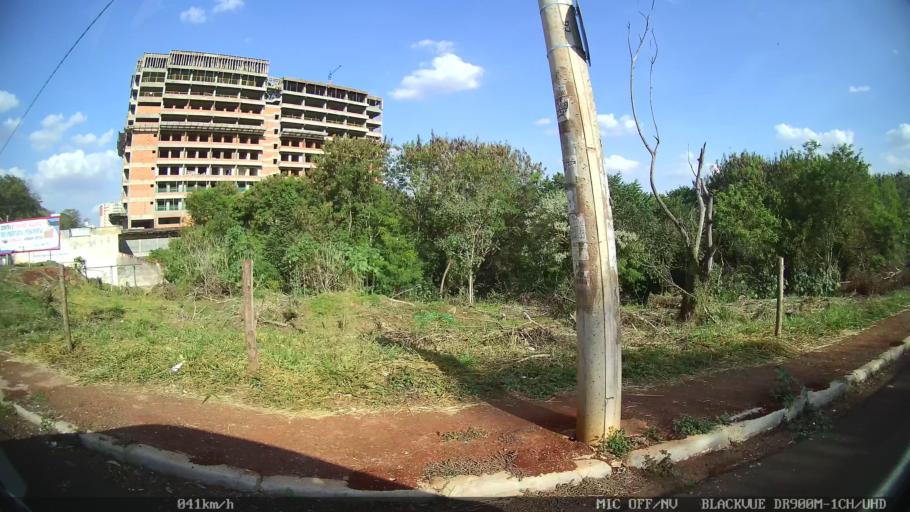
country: BR
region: Sao Paulo
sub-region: Ribeirao Preto
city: Ribeirao Preto
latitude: -21.1731
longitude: -47.8440
